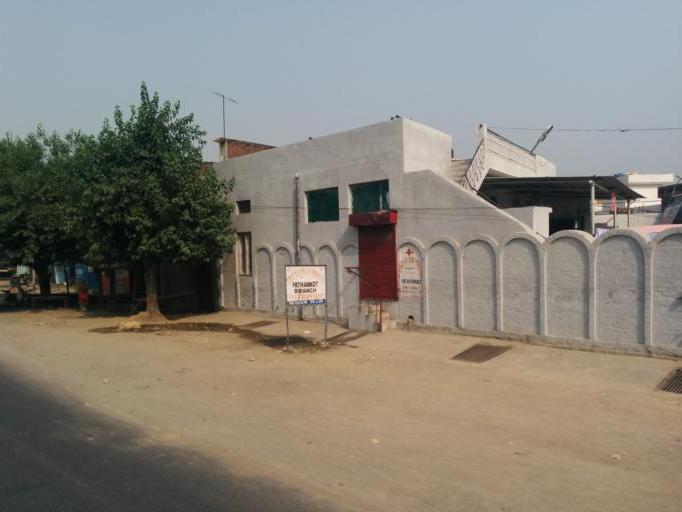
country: IN
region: Punjab
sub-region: Pathankot
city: Pathankot
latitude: 32.2560
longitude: 75.6583
